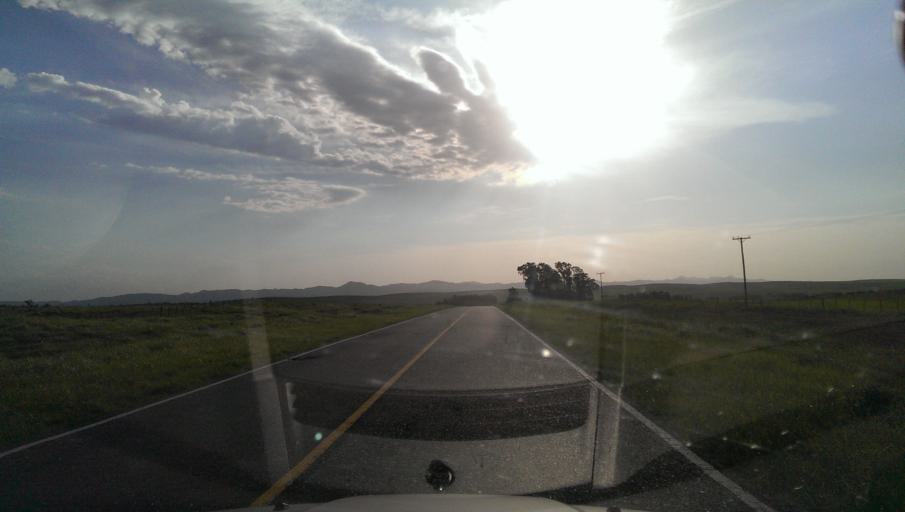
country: AR
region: Buenos Aires
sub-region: Partido de Coronel Suarez
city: Coronel Suarez
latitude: -37.8317
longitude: -61.8294
